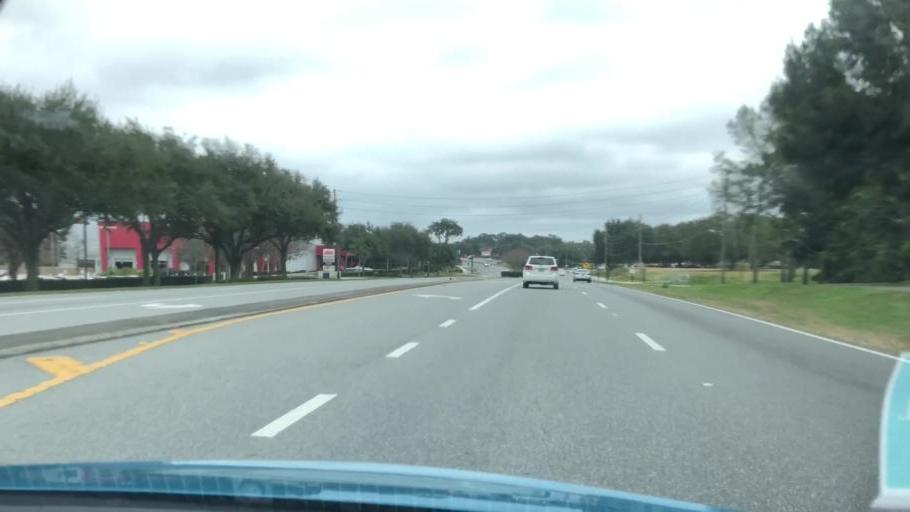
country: US
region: Florida
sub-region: Seminole County
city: Lake Mary
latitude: 28.7937
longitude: -81.3384
